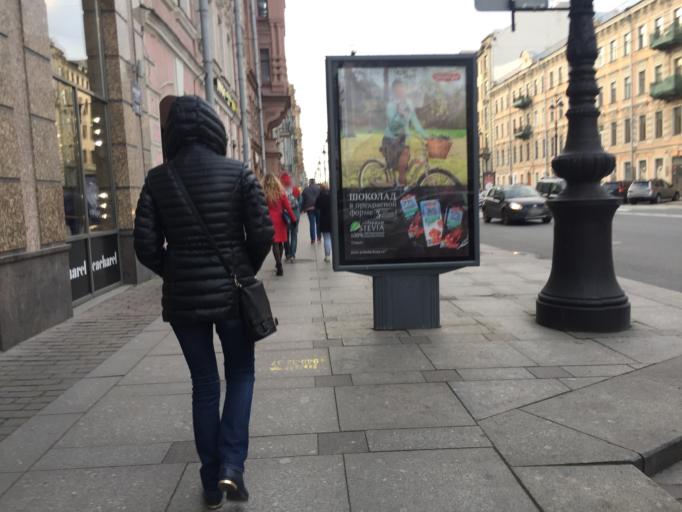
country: RU
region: St.-Petersburg
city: Centralniy
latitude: 59.9268
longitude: 30.3758
